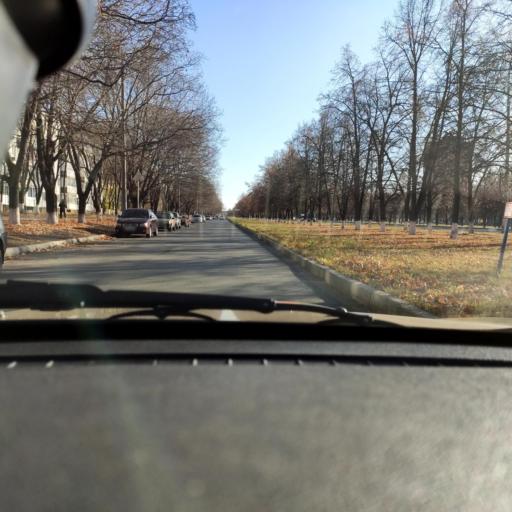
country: RU
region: Samara
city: Tol'yatti
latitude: 53.5197
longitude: 49.2854
